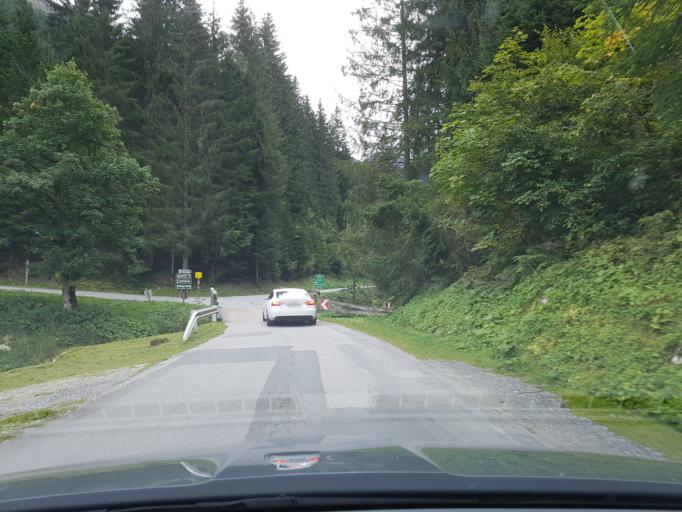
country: AT
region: Salzburg
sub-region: Politischer Bezirk Sankt Johann im Pongau
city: Forstau
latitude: 47.3563
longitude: 13.5689
